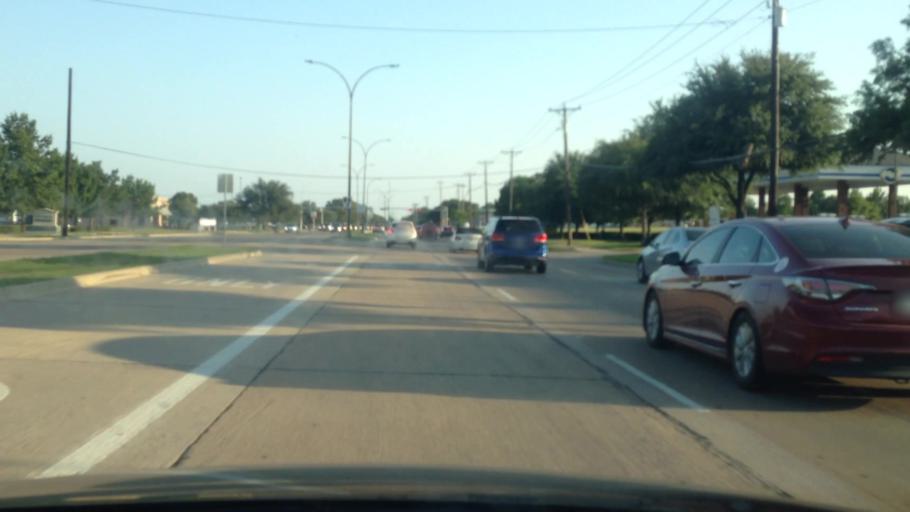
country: US
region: Texas
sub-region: Tarrant County
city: Dalworthington Gardens
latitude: 32.6727
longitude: -97.1150
